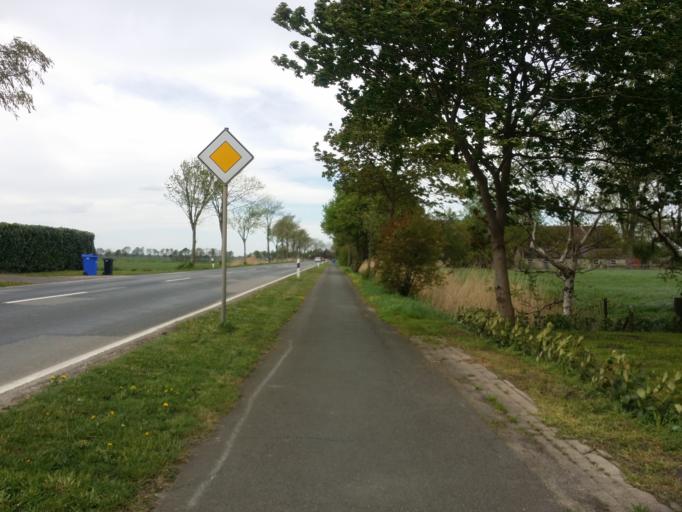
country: DE
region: Lower Saxony
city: Lemwerder
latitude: 53.1437
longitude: 8.5614
